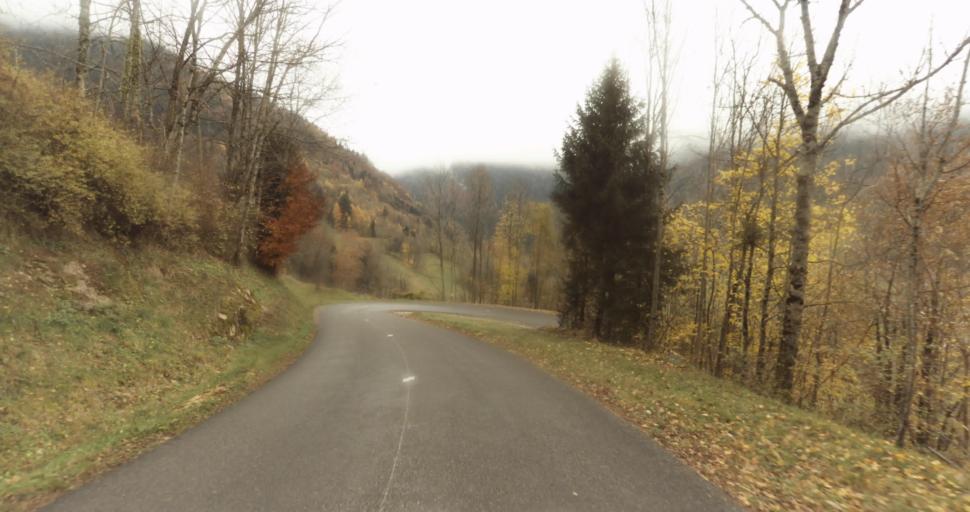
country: FR
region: Rhone-Alpes
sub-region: Departement de la Haute-Savoie
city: Thorens-Glieres
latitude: 45.9726
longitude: 6.2901
